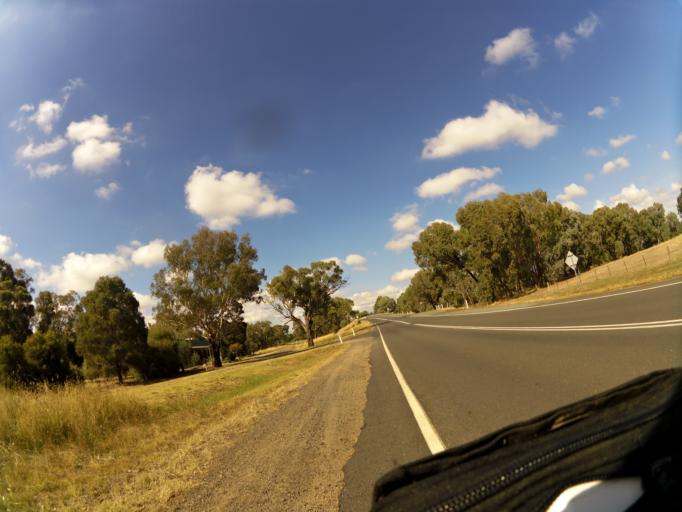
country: AU
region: Victoria
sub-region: Benalla
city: Benalla
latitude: -36.5709
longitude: 145.9923
